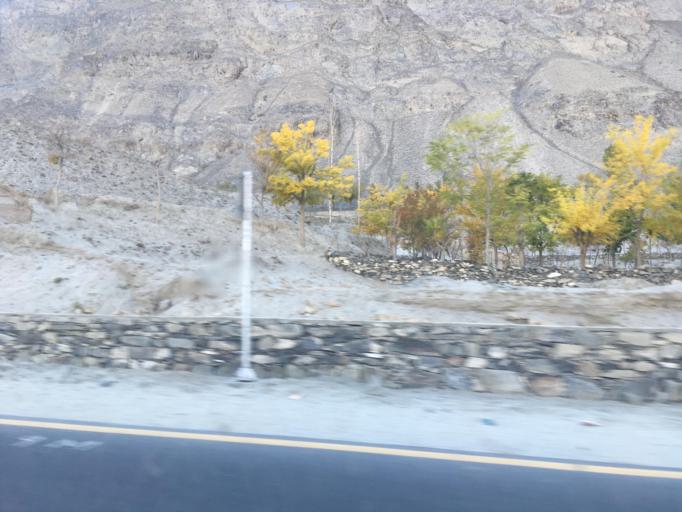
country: PK
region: Gilgit-Baltistan
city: Skardu
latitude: 35.3620
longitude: 75.5060
